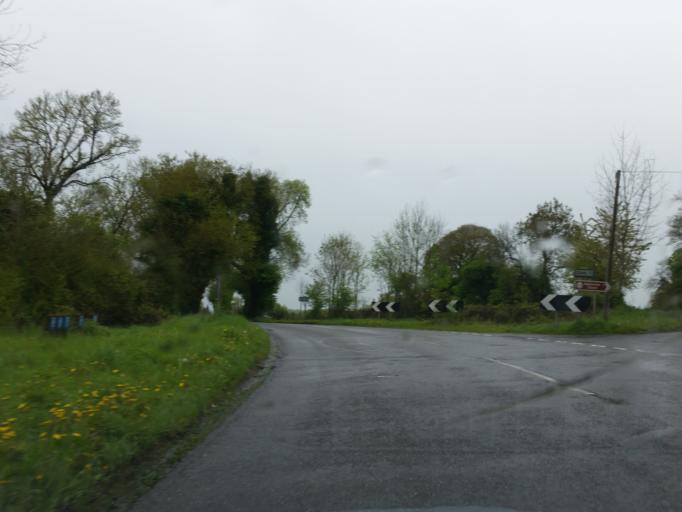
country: GB
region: Northern Ireland
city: Lisnaskea
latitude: 54.2171
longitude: -7.4647
